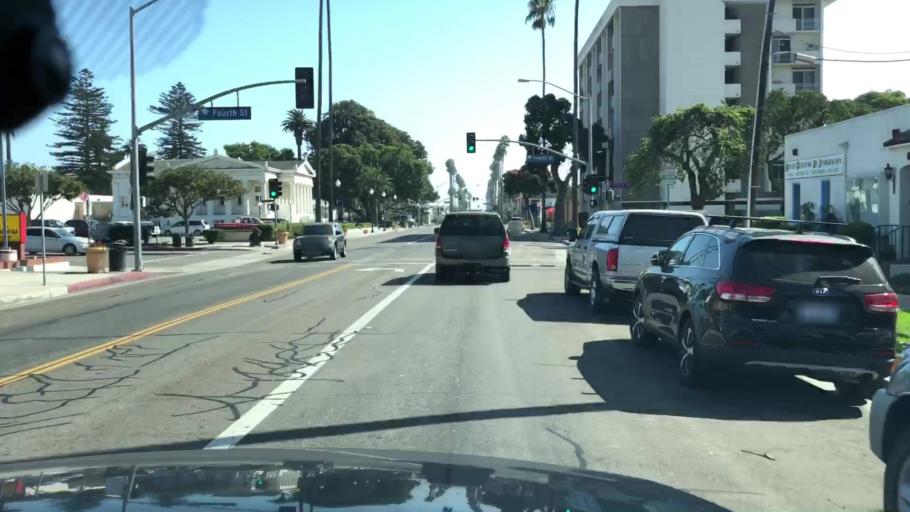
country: US
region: California
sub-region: Ventura County
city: Oxnard
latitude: 34.1994
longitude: -119.1812
